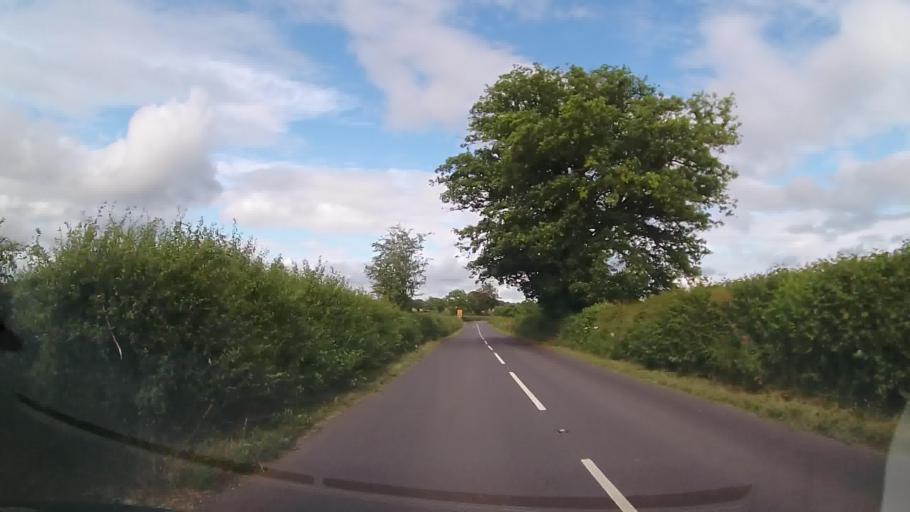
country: GB
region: England
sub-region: Shropshire
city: Petton
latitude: 52.8627
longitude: -2.7803
